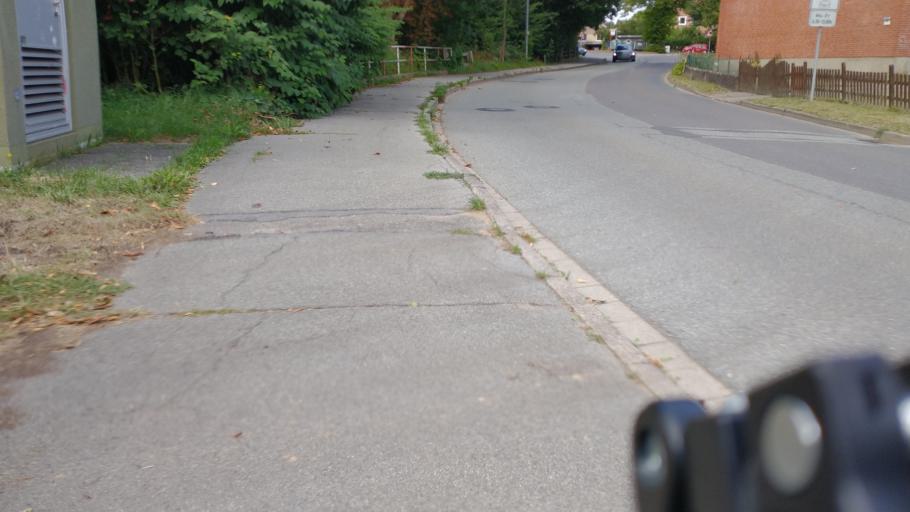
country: DE
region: Schleswig-Holstein
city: Rumpel
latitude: 53.8127
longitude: 10.3416
